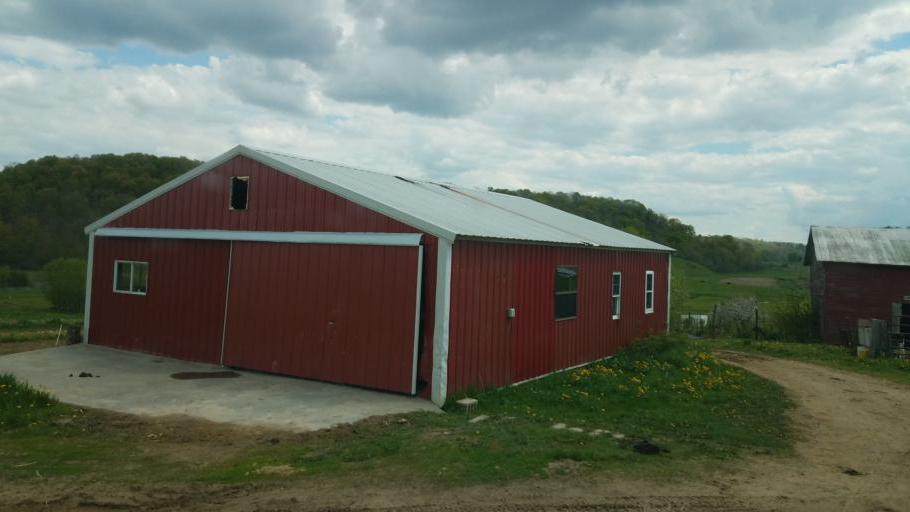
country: US
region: Wisconsin
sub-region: Vernon County
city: Hillsboro
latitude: 43.6171
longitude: -90.3898
